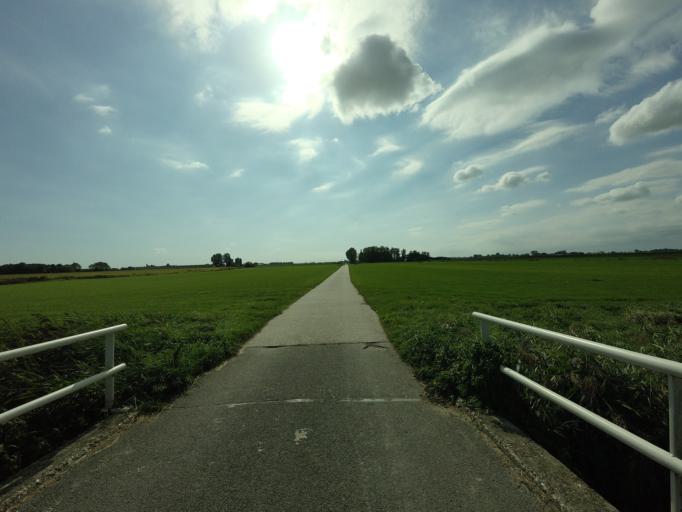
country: NL
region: Friesland
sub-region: Gemeente Littenseradiel
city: Makkum
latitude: 53.0880
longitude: 5.6344
